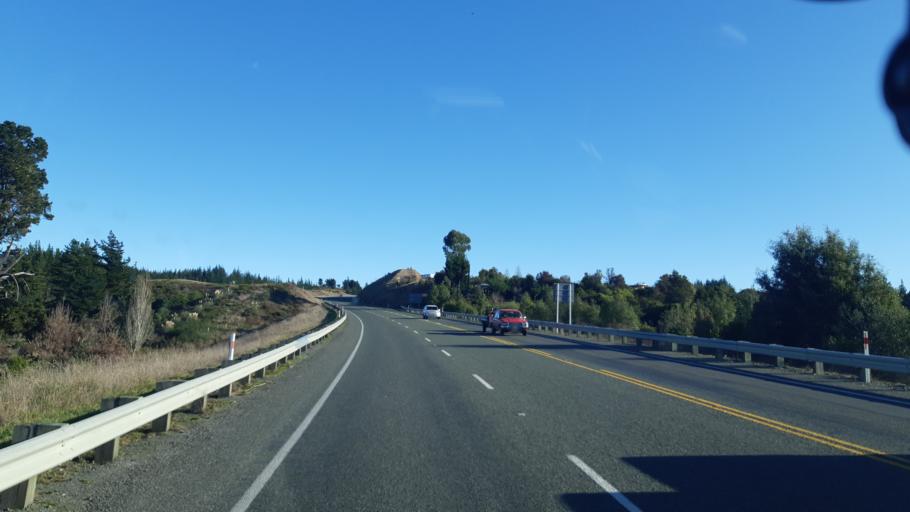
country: NZ
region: Tasman
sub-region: Tasman District
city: Mapua
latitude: -41.2497
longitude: 173.0660
